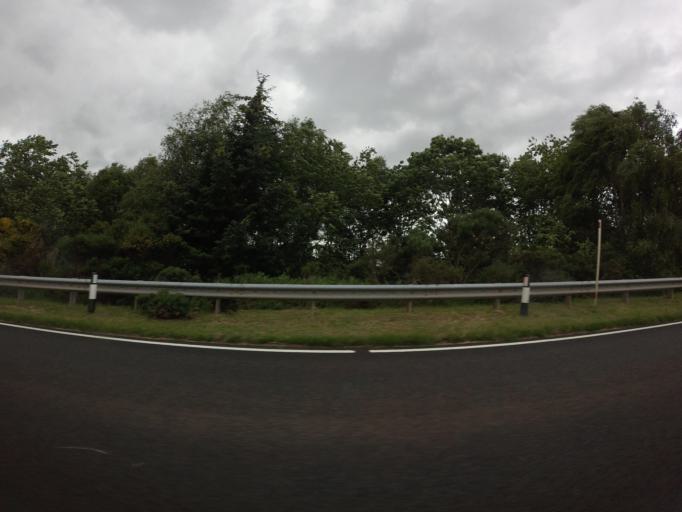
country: GB
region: Scotland
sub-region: Highland
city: Muir of Ord
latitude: 57.6255
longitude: -4.7000
